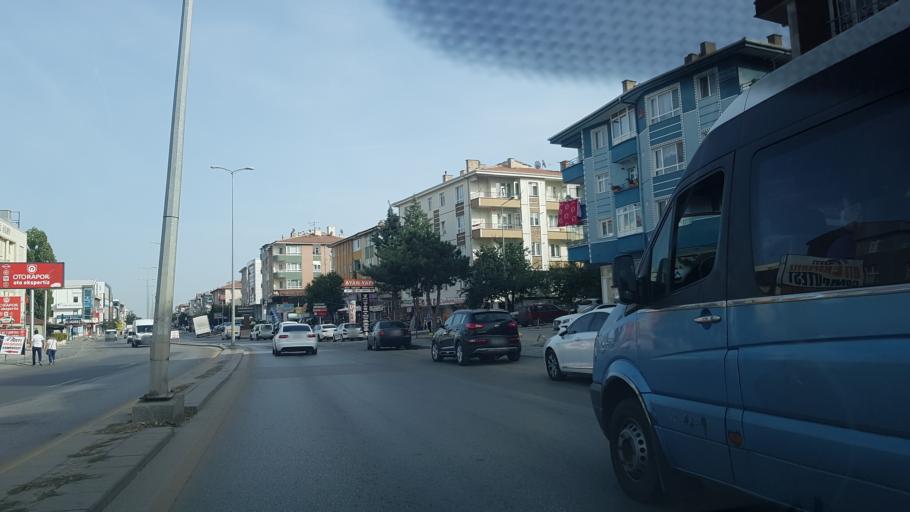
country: TR
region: Ankara
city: Etimesgut
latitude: 39.9511
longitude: 32.6496
